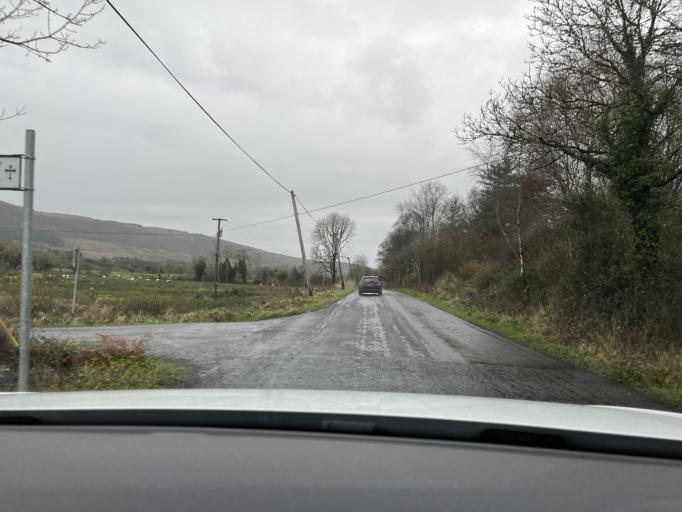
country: IE
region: Connaught
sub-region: County Leitrim
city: Manorhamilton
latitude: 54.2847
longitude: -8.2088
